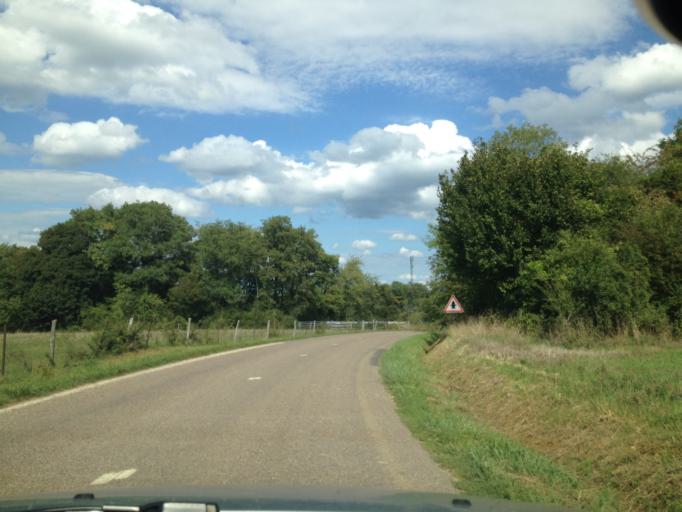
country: FR
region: Franche-Comte
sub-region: Departement de la Haute-Saone
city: Saint-Loup-sur-Semouse
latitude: 47.9310
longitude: 6.1546
